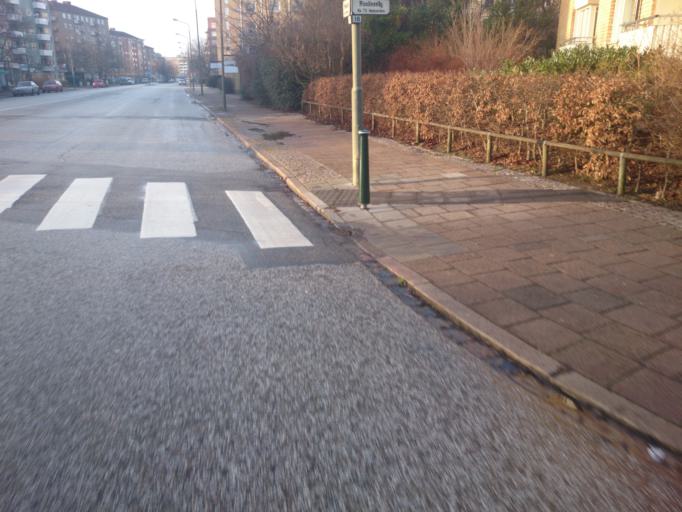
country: SE
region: Skane
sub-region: Malmo
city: Malmoe
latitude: 55.6019
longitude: 12.9782
